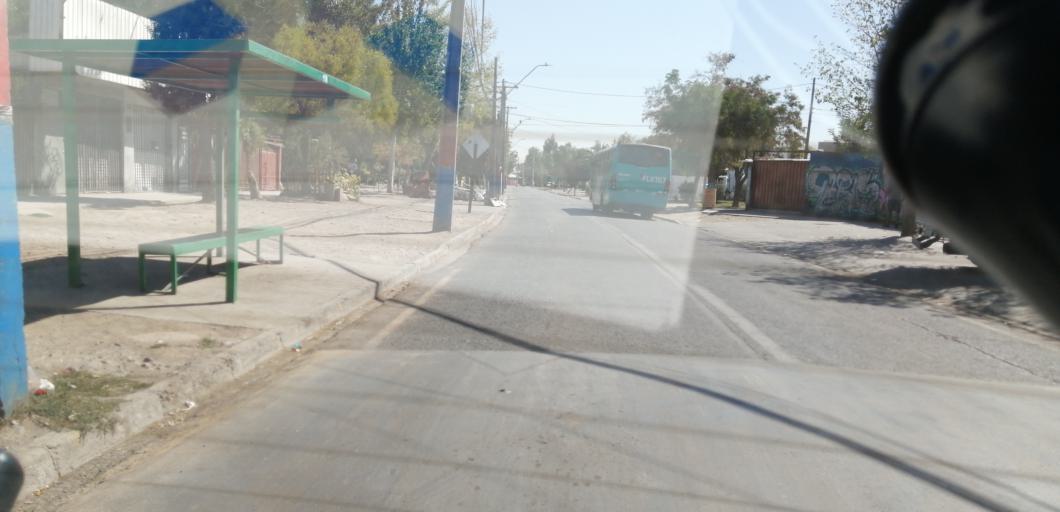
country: CL
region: Santiago Metropolitan
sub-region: Provincia de Santiago
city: Lo Prado
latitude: -33.4394
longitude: -70.7580
